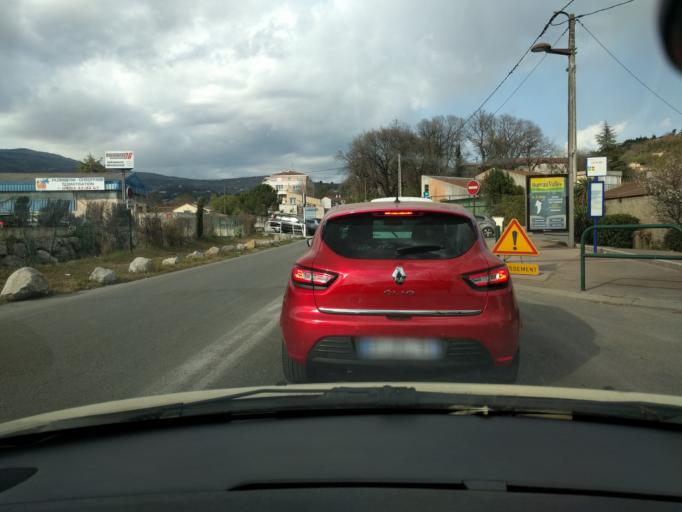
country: FR
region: Provence-Alpes-Cote d'Azur
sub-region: Departement des Alpes-Maritimes
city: Mouans-Sartoux
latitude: 43.6408
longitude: 6.9568
